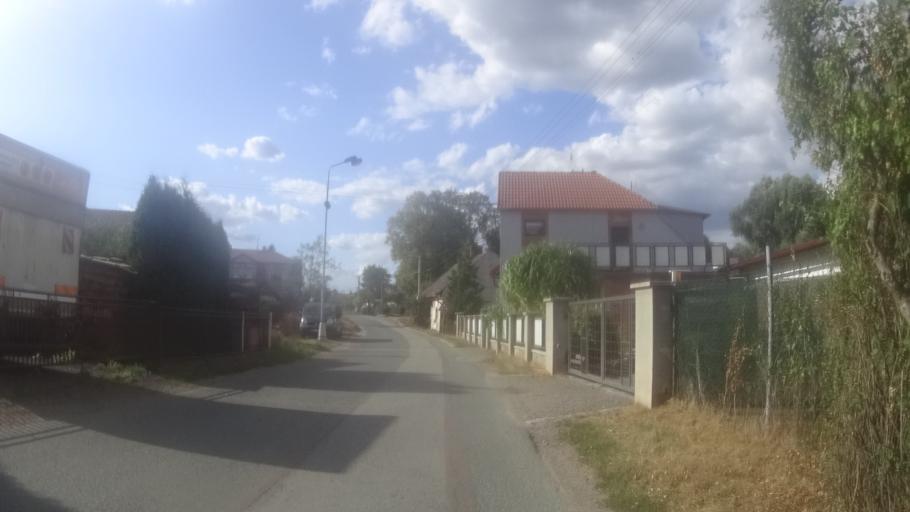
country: CZ
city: Albrechtice nad Orlici
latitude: 50.1478
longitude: 16.0602
